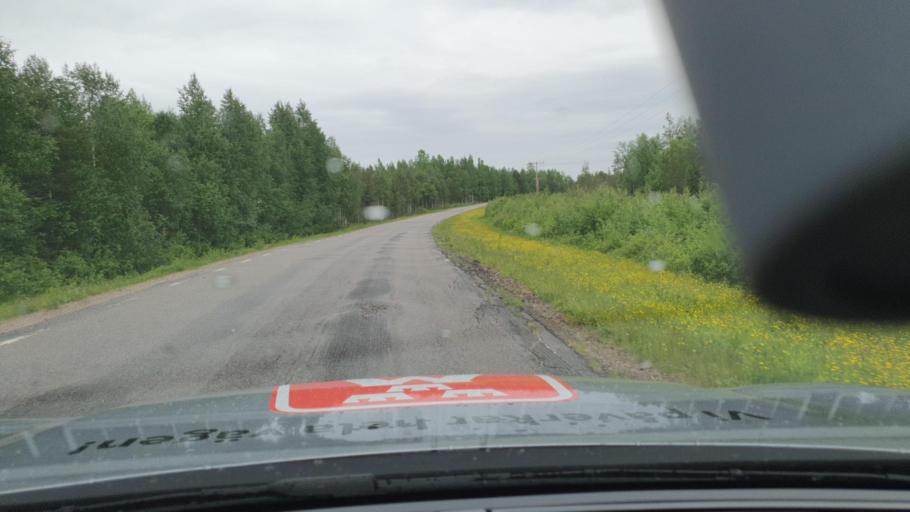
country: SE
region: Norrbotten
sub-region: Pajala Kommun
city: Pajala
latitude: 66.7462
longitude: 23.1700
